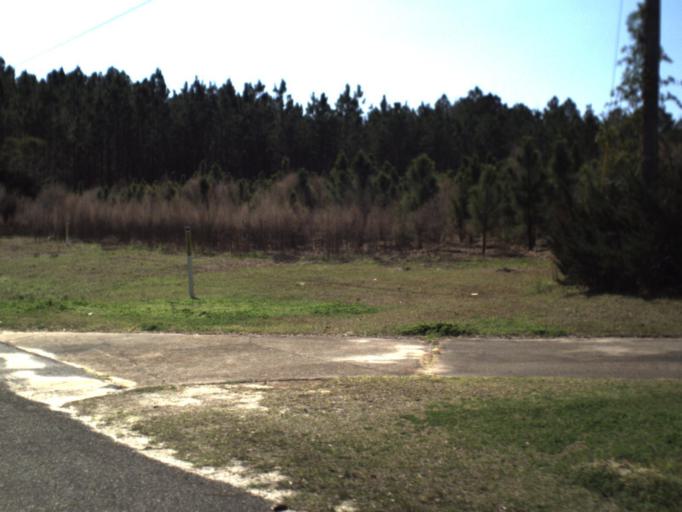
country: US
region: Florida
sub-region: Calhoun County
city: Blountstown
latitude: 30.4627
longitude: -85.0449
